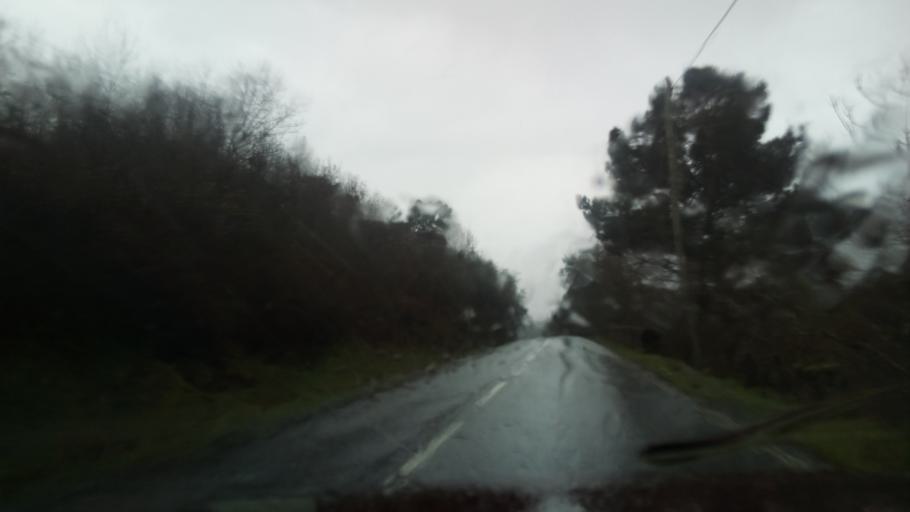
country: PT
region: Guarda
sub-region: Fornos de Algodres
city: Fornos de Algodres
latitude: 40.6202
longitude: -7.4824
